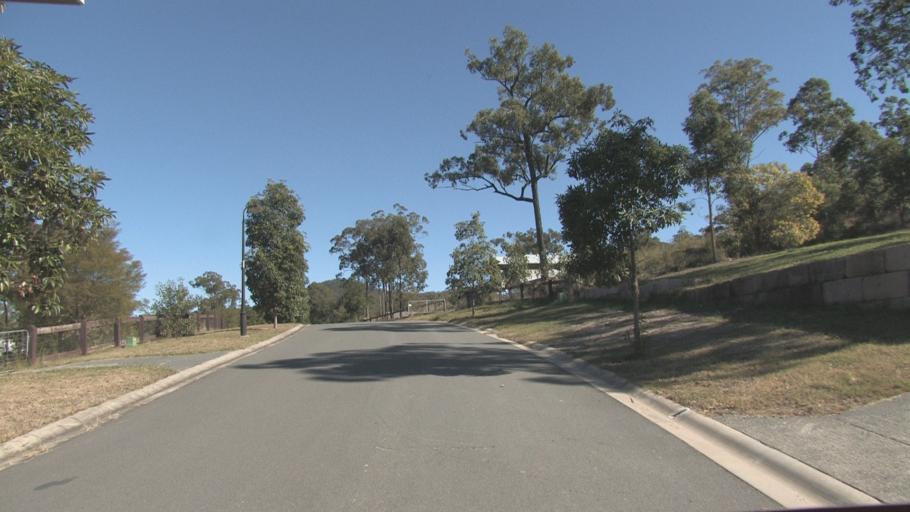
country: AU
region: Queensland
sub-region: Ipswich
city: Springfield Lakes
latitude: -27.7226
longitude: 152.9109
